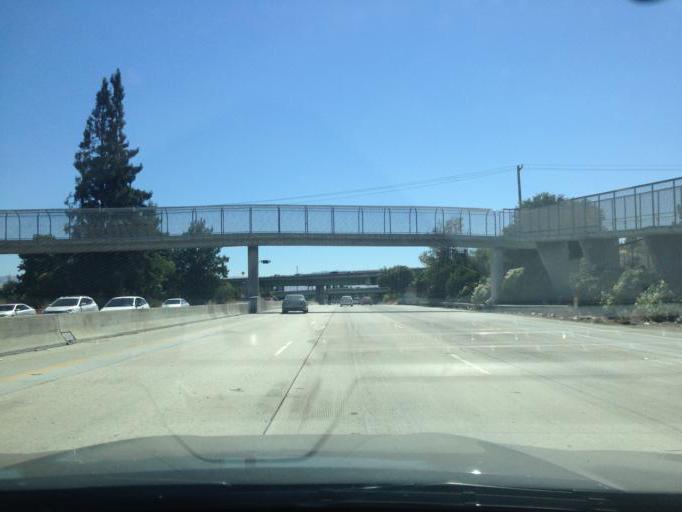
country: US
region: California
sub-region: Santa Clara County
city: Burbank
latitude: 37.3169
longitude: -121.9442
